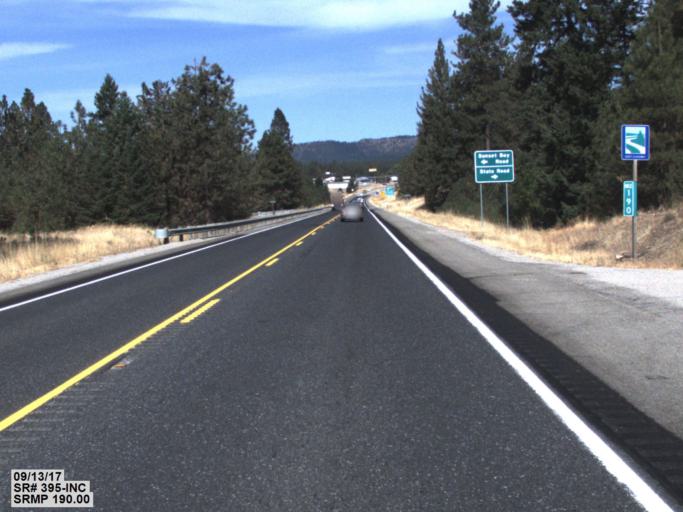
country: US
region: Washington
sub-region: Spokane County
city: Deer Park
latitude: 48.0527
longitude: -117.6145
